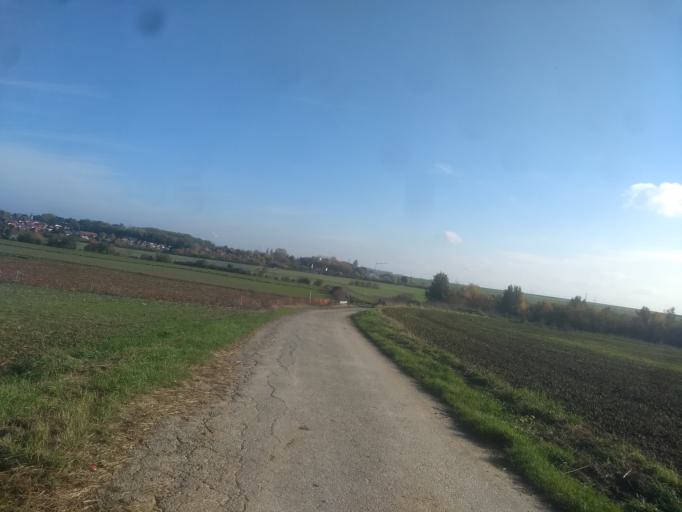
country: FR
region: Nord-Pas-de-Calais
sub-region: Departement du Pas-de-Calais
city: Tilloy-les-Mofflaines
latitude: 50.2766
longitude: 2.8019
